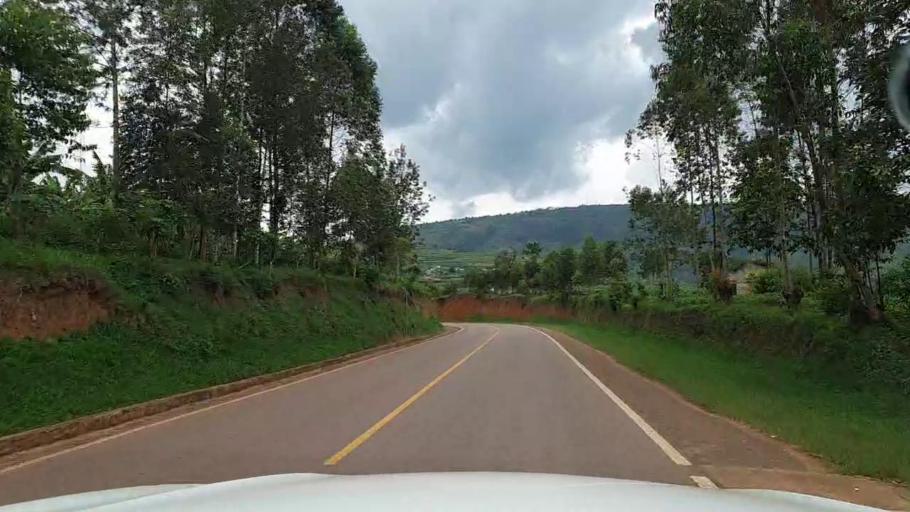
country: RW
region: Kigali
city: Kigali
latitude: -1.7825
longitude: 30.1303
